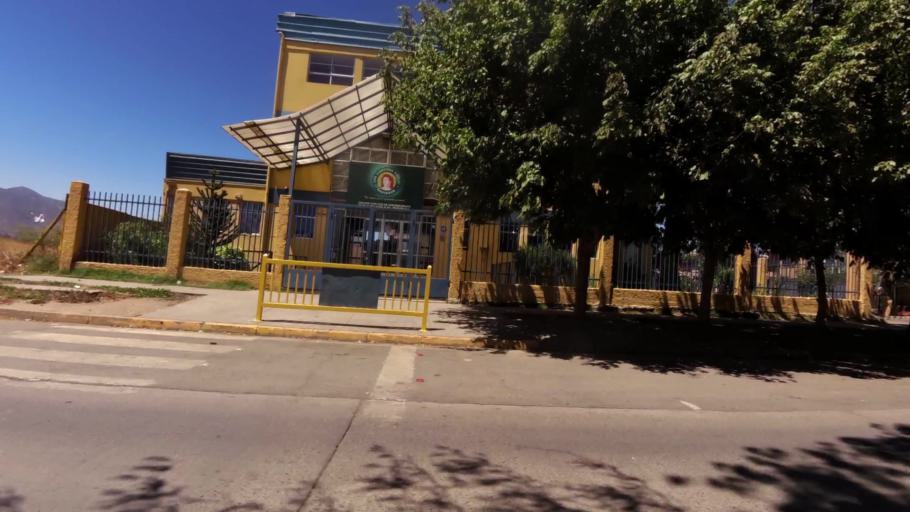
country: CL
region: O'Higgins
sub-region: Provincia de Cachapoal
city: Rancagua
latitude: -34.1603
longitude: -70.7038
